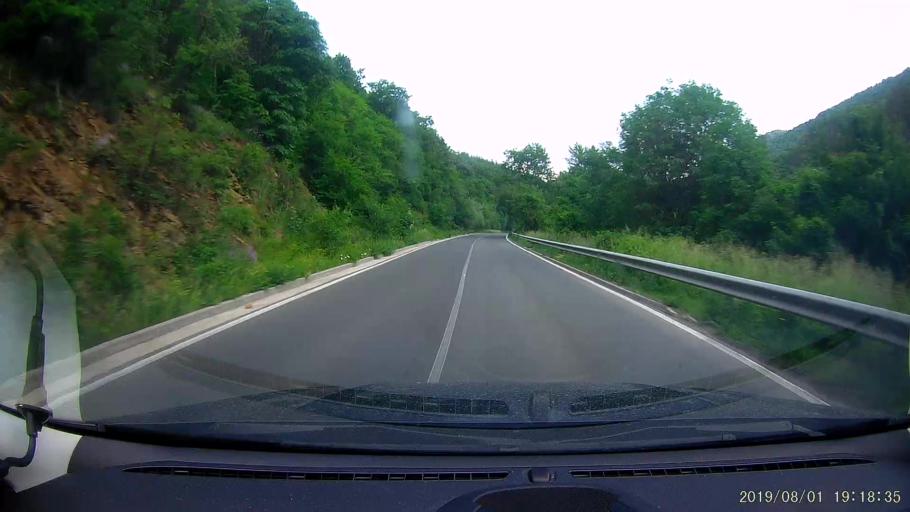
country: BG
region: Shumen
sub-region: Obshtina Smyadovo
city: Smyadovo
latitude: 42.9110
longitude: 26.9398
